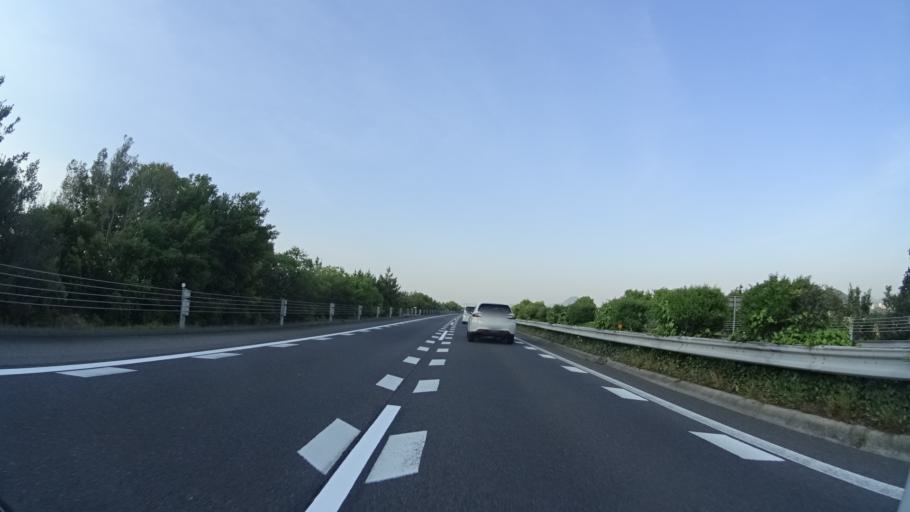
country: JP
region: Kagawa
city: Tadotsu
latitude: 34.2336
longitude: 133.7496
